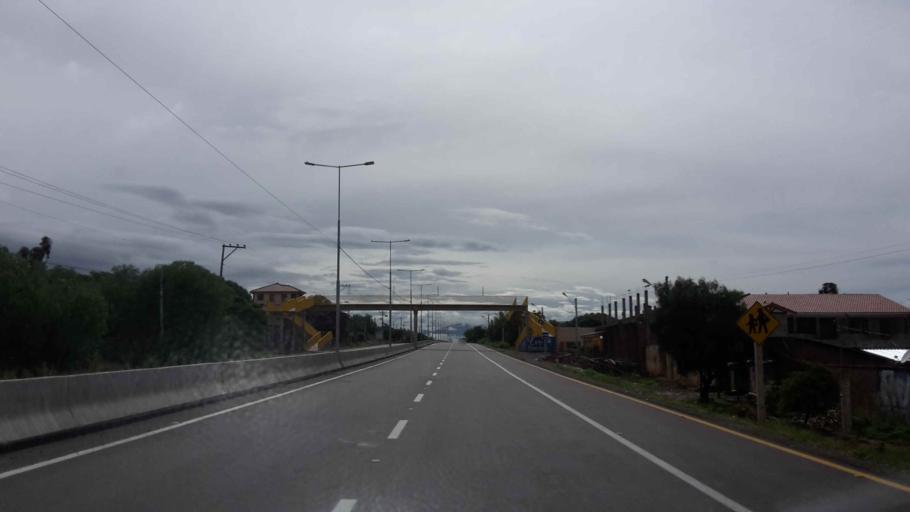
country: BO
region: Cochabamba
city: Tarata
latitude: -17.5420
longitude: -66.0342
